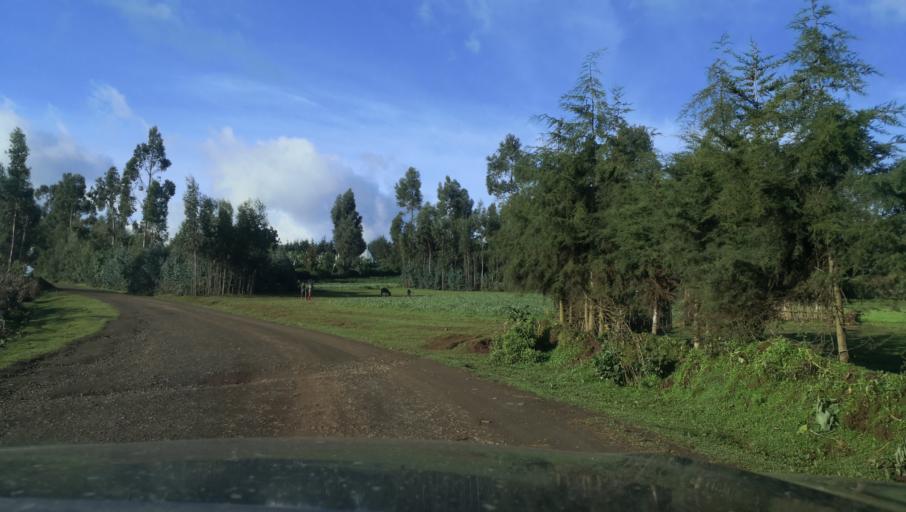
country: ET
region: Southern Nations, Nationalities, and People's Region
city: Butajira
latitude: 8.3909
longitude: 38.3077
